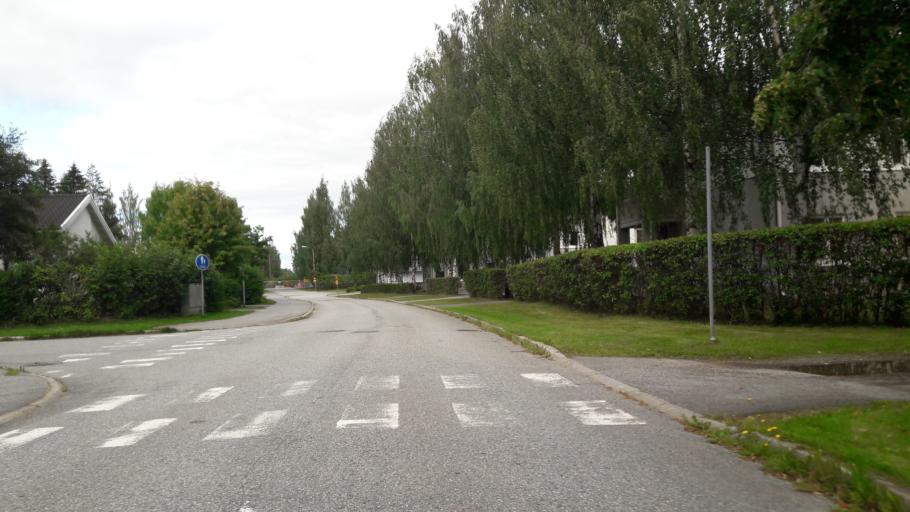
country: FI
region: North Karelia
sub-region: Joensuu
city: Joensuu
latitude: 62.5877
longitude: 29.8050
